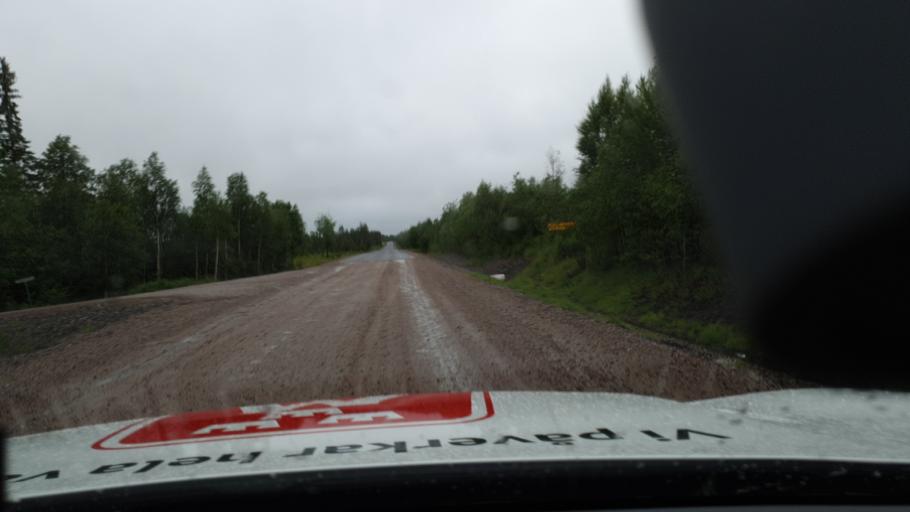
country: SE
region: Norrbotten
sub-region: Overtornea Kommun
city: OEvertornea
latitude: 66.5306
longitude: 23.3682
